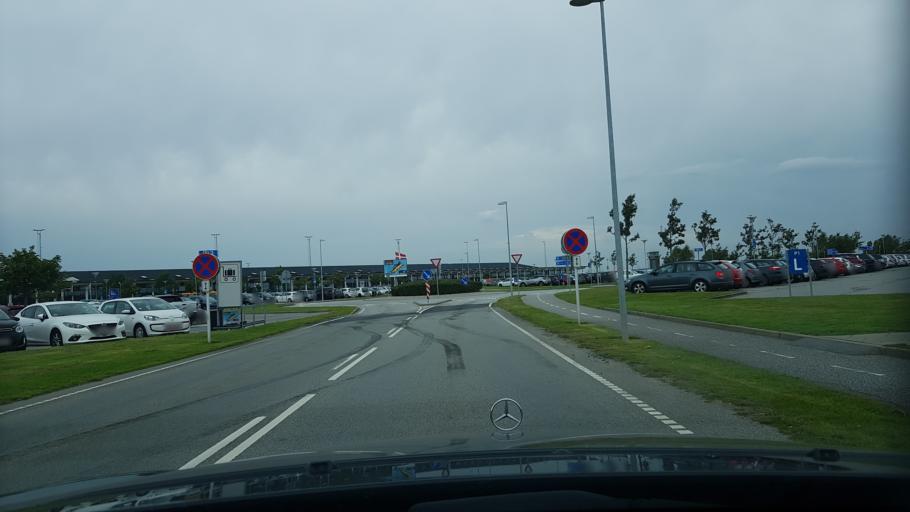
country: DK
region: North Denmark
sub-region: Alborg Kommune
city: Vadum
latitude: 57.0862
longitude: 9.8762
